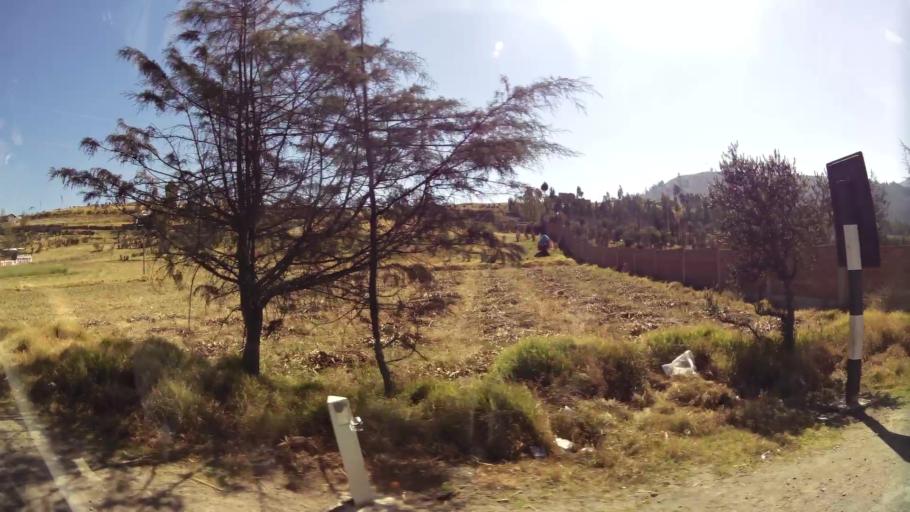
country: PE
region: Junin
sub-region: Provincia de Concepcion
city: Concepcion
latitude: -11.9376
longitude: -75.3113
